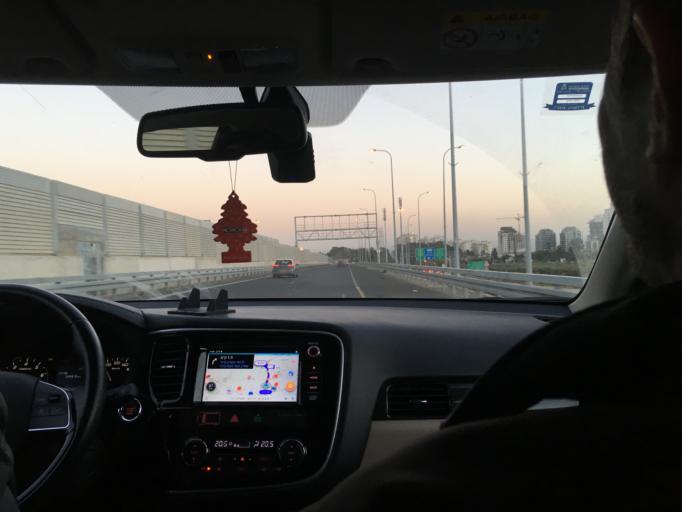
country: IL
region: Central District
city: Kfar Saba
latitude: 32.1714
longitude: 34.8975
